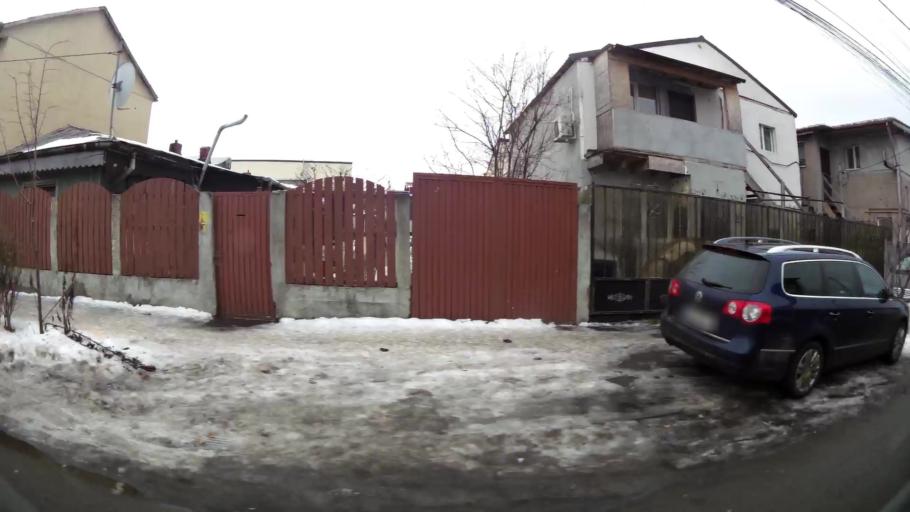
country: RO
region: Ilfov
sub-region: Comuna Pantelimon
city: Pantelimon
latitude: 44.4343
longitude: 26.1973
